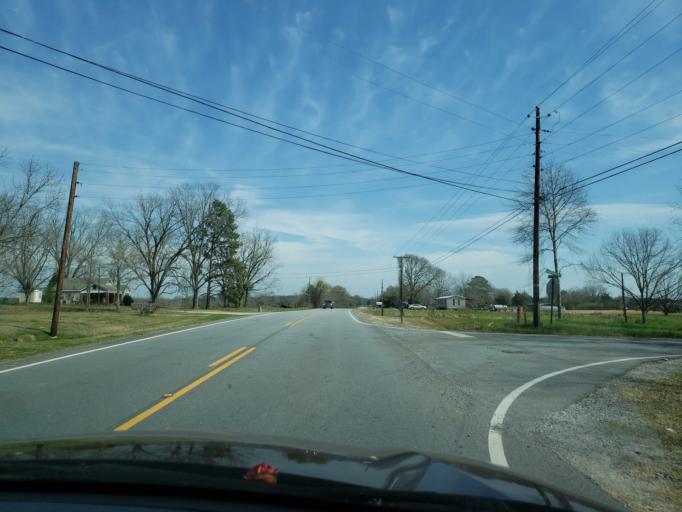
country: US
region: Alabama
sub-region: Elmore County
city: Tallassee
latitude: 32.5598
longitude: -85.8069
